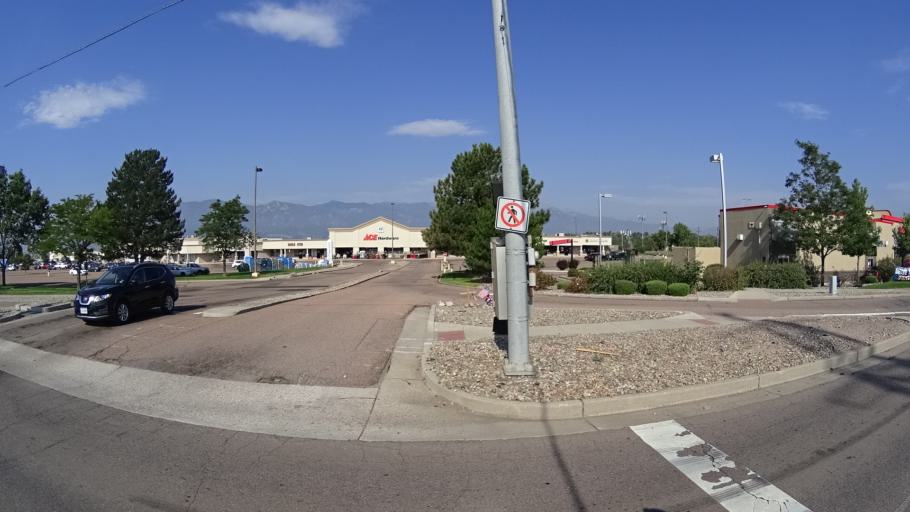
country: US
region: Colorado
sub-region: El Paso County
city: Stratmoor
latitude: 38.7932
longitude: -104.7577
